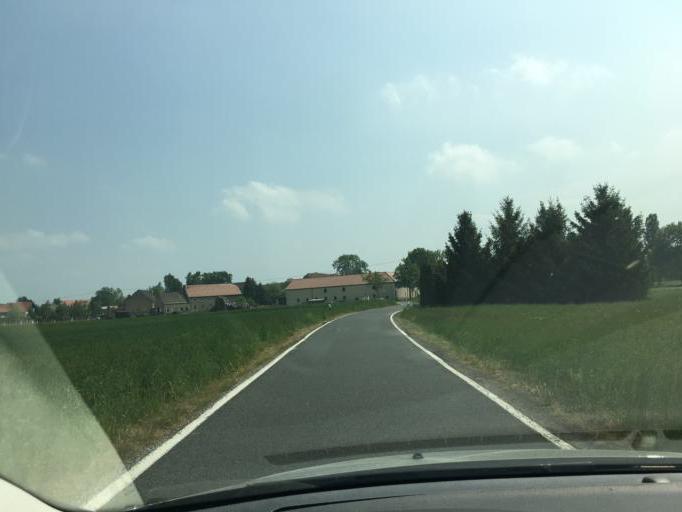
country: DE
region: Saxony
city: Otterwisch
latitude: 51.1860
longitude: 12.6573
